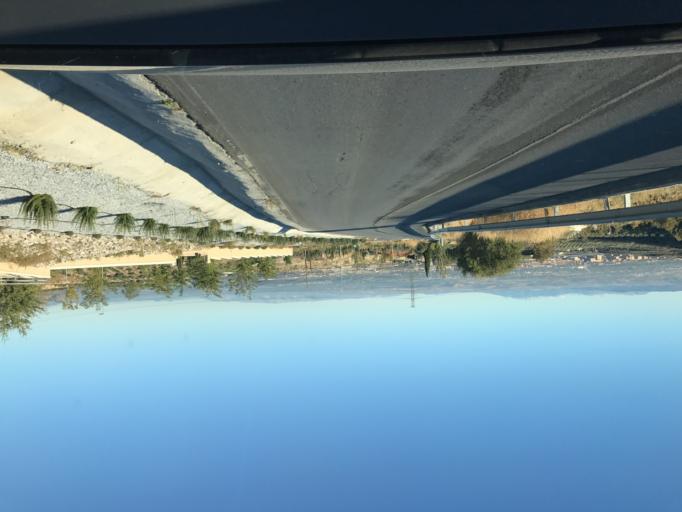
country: ES
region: Andalusia
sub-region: Provincia de Granada
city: Alfacar
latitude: 37.2295
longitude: -3.5735
